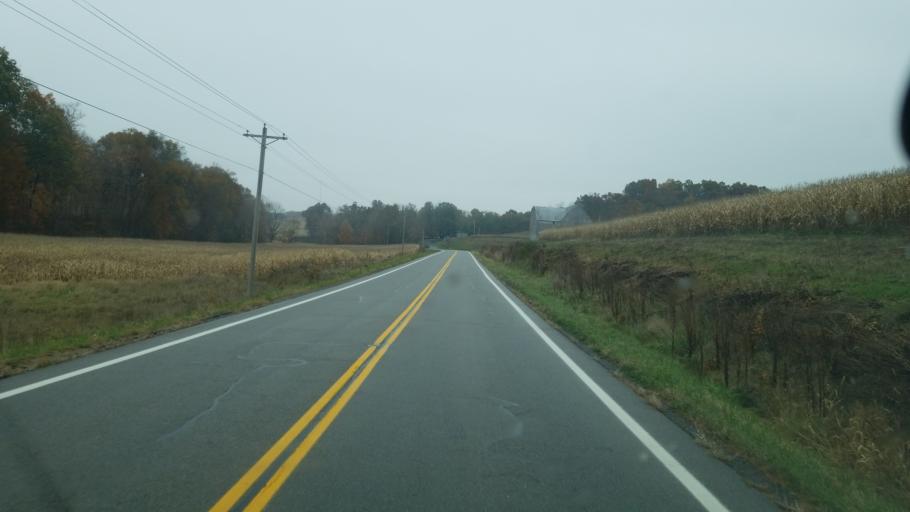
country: US
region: Ohio
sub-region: Coshocton County
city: Coshocton
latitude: 40.3941
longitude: -81.8705
